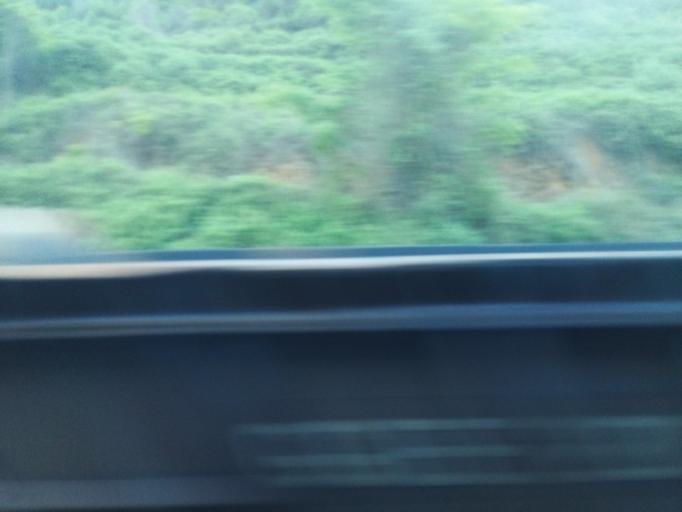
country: BR
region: Minas Gerais
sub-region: Resplendor
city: Resplendor
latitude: -19.3991
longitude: -41.1628
